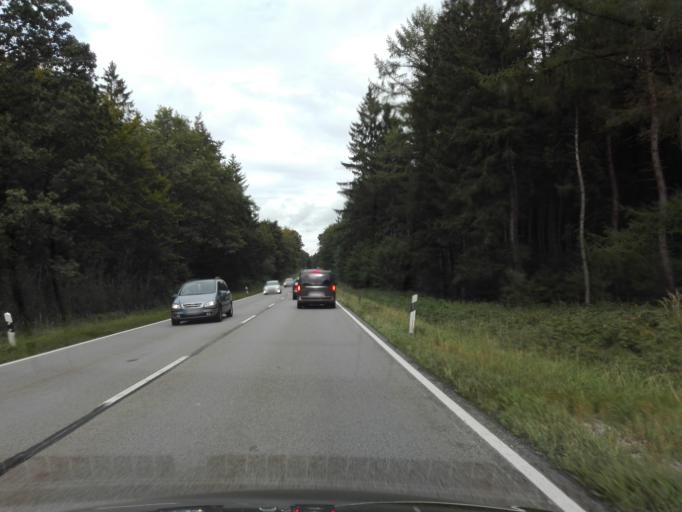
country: DE
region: Bavaria
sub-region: Upper Bavaria
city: Maitenbeth
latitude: 48.1460
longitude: 12.0724
